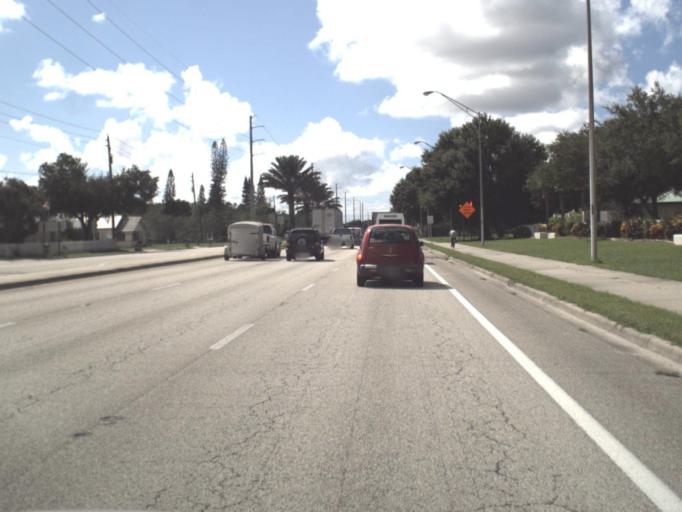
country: US
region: Florida
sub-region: Manatee County
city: Samoset
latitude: 27.4476
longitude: -82.5371
